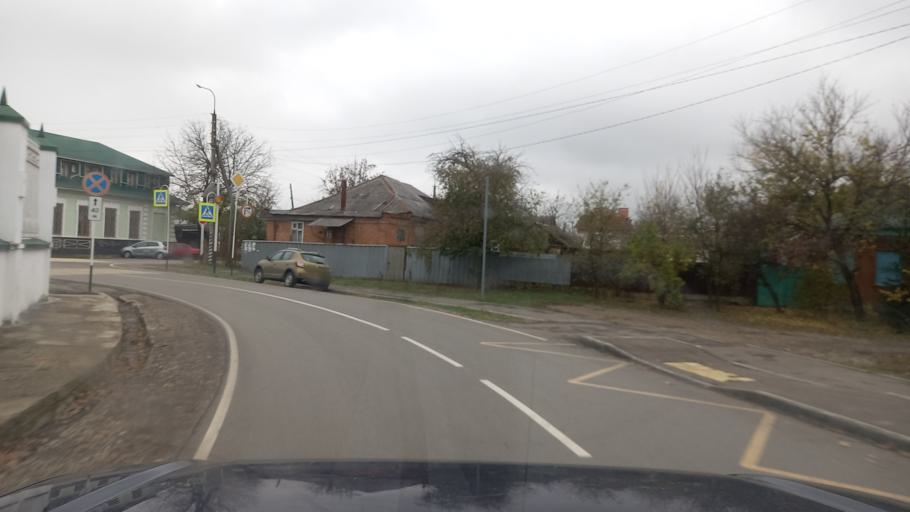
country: RU
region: Adygeya
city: Maykop
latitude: 44.6007
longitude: 40.0783
